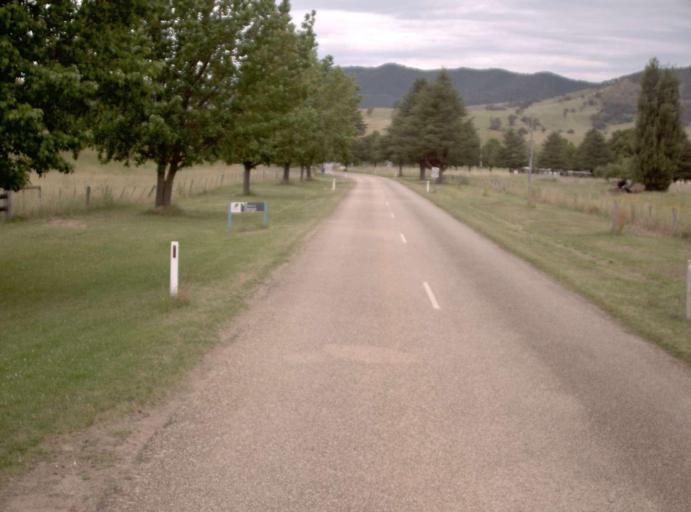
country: AU
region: Victoria
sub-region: East Gippsland
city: Bairnsdale
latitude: -37.4714
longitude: 147.2502
